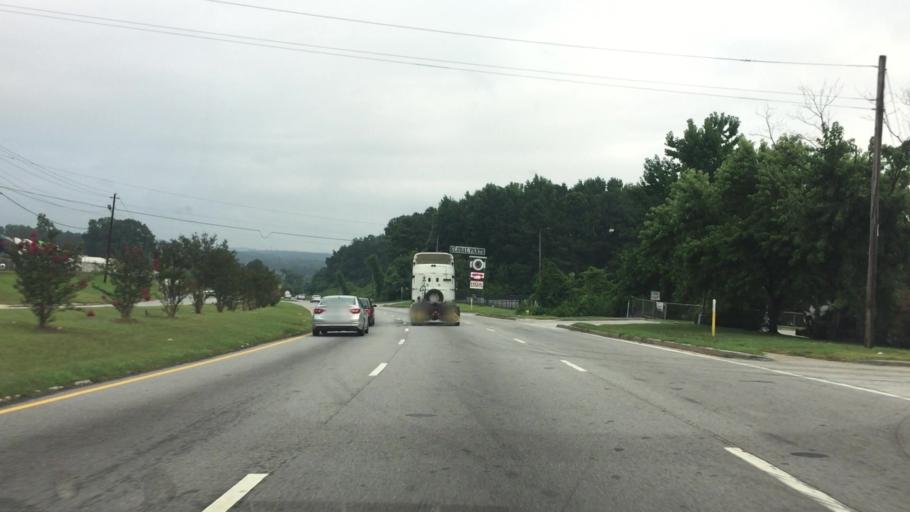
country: US
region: Georgia
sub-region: Clayton County
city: Conley
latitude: 33.6717
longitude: -84.3409
